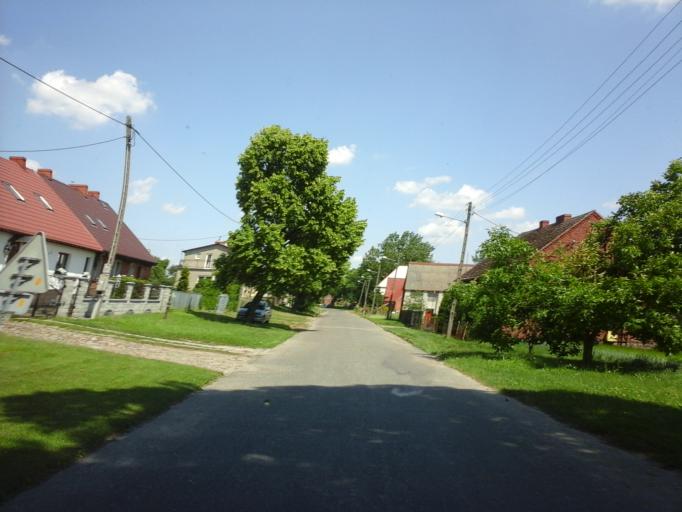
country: PL
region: West Pomeranian Voivodeship
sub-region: Powiat choszczenski
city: Choszczno
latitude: 53.1425
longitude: 15.3468
